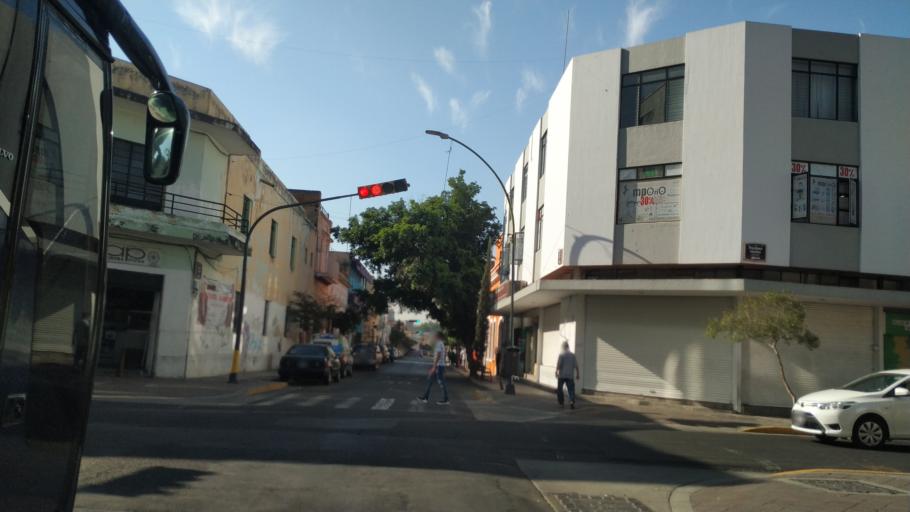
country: MX
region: Jalisco
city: Guadalajara
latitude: 20.6729
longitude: -103.3507
